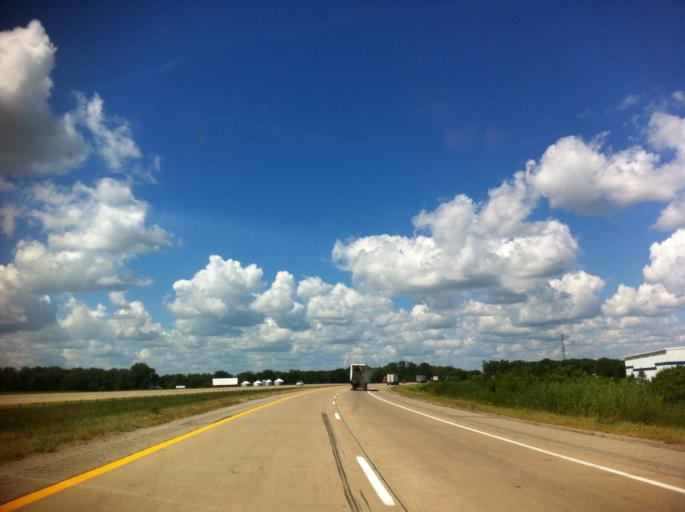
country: US
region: Michigan
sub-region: Monroe County
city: Dundee
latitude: 41.9727
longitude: -83.6775
